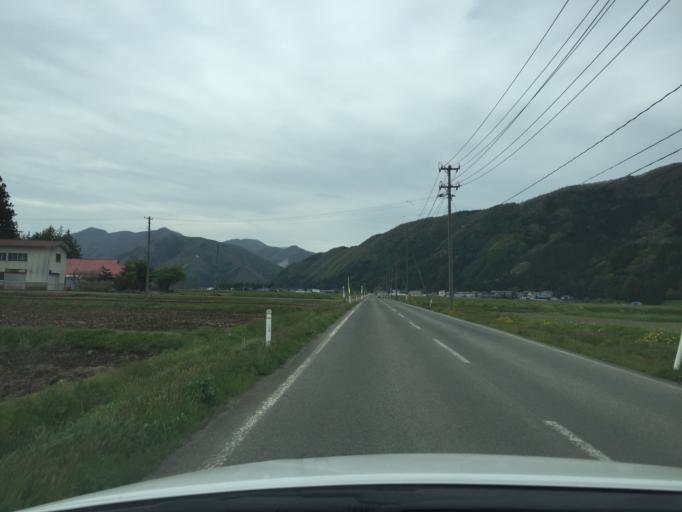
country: JP
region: Fukushima
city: Inawashiro
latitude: 37.5834
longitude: 140.1379
